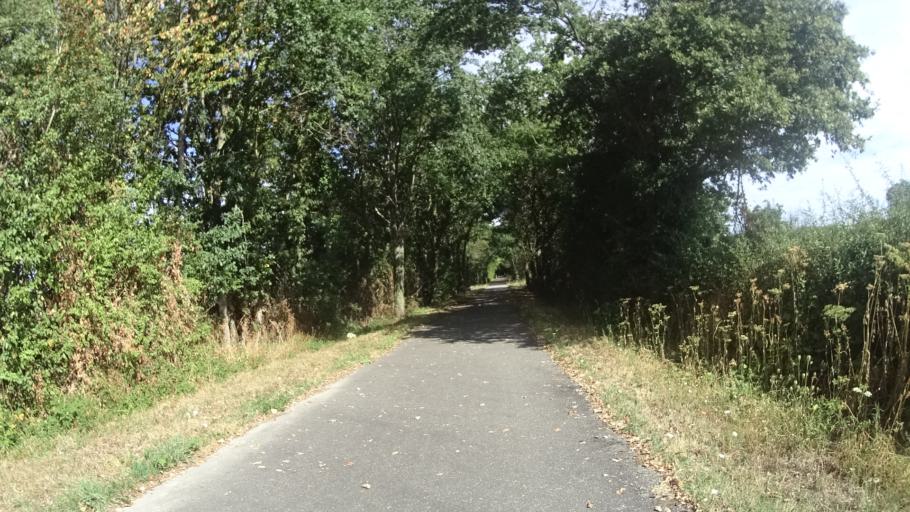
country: FR
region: Bourgogne
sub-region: Departement de Saone-et-Loire
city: Bourbon-Lancy
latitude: 46.6170
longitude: 3.7412
